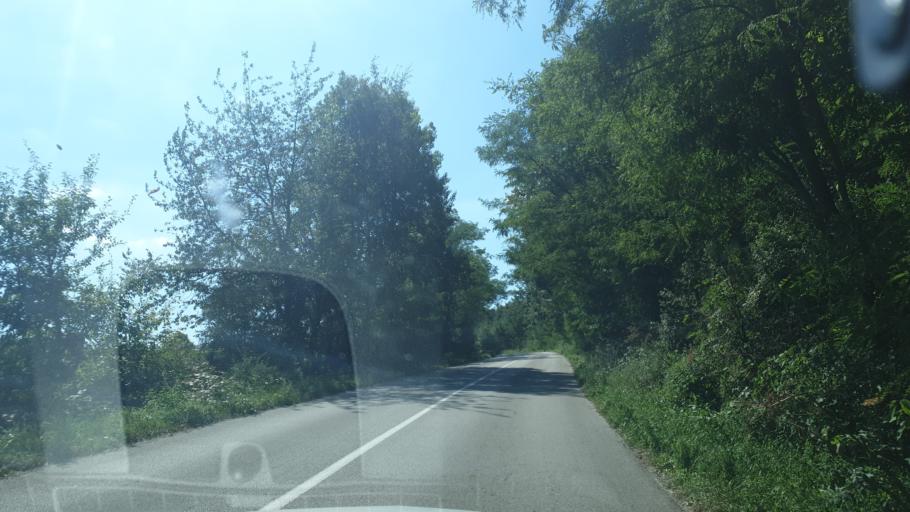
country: RS
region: Central Serbia
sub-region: Zlatiborski Okrug
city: Kosjeric
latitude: 44.0405
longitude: 20.0191
